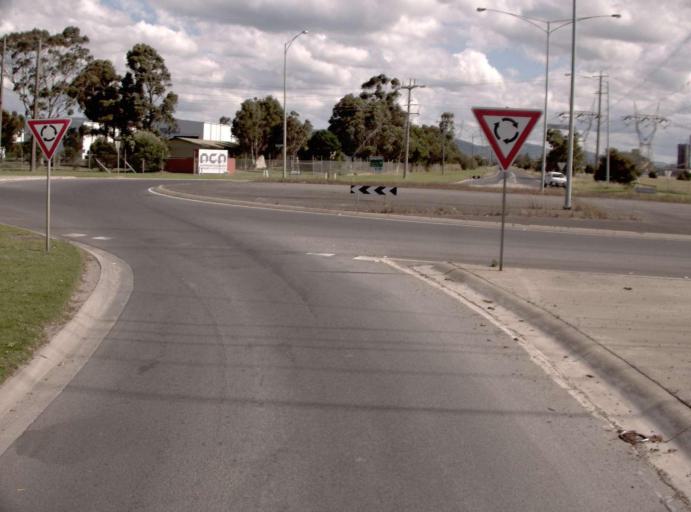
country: AU
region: Victoria
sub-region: Latrobe
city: Morwell
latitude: -38.2481
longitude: 146.4362
